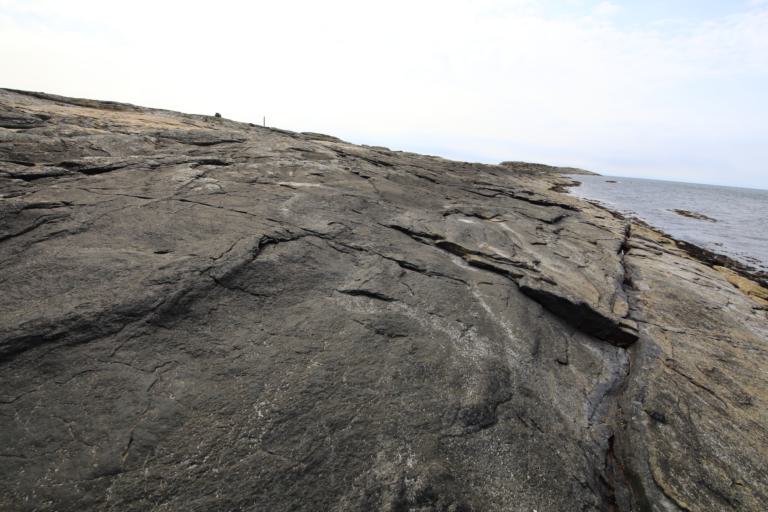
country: SE
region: Halland
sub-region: Kungsbacka Kommun
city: Frillesas
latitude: 57.2580
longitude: 12.0966
